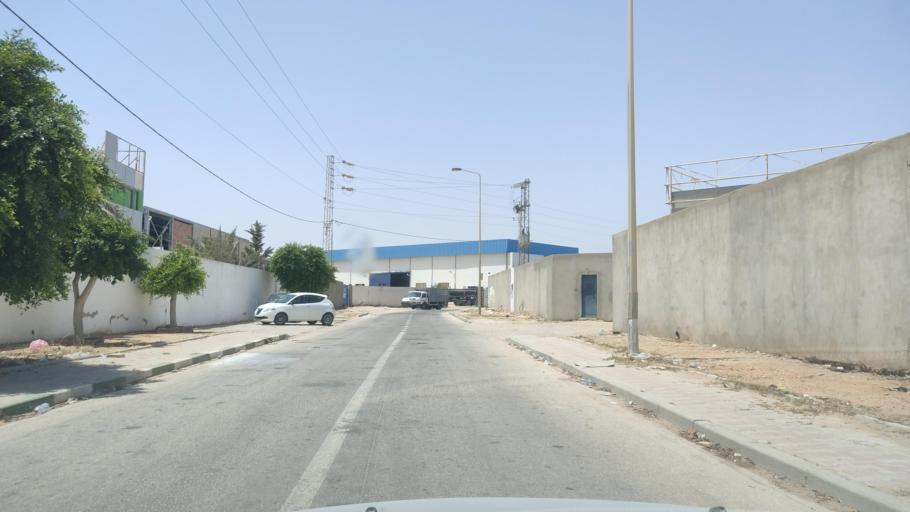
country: TN
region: Safaqis
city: Sfax
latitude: 34.6596
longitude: 10.6980
